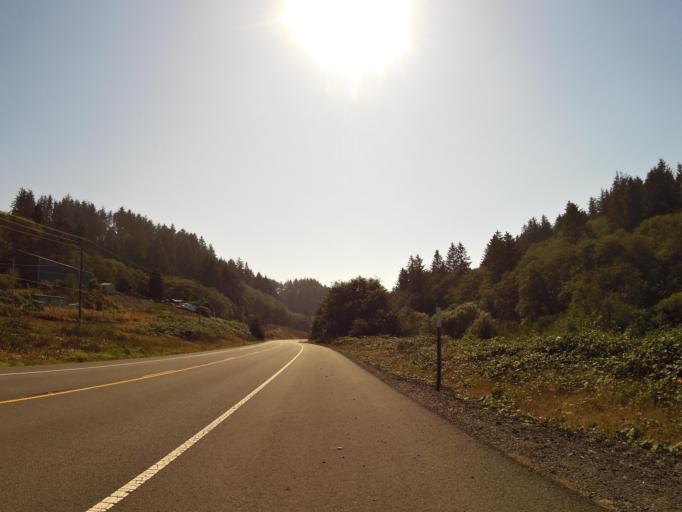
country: US
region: Oregon
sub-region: Tillamook County
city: Pacific City
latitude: 45.1534
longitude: -123.9554
